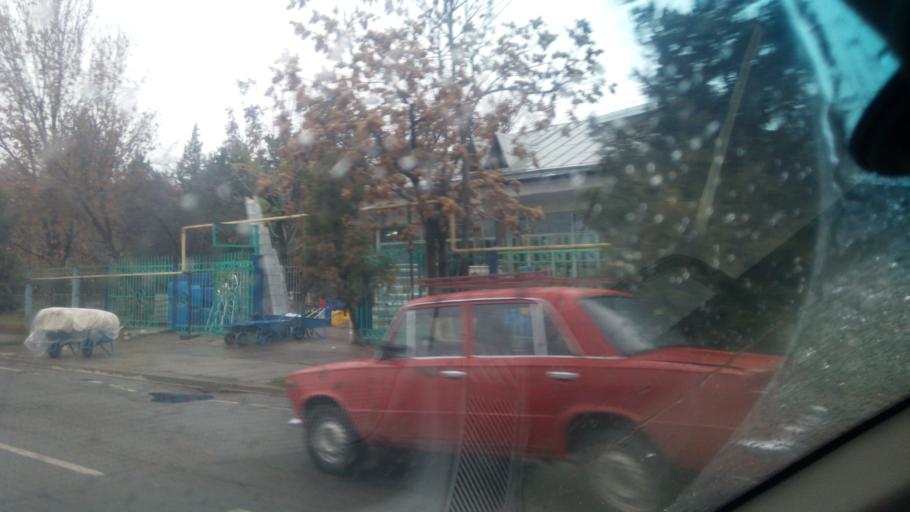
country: UZ
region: Toshkent Shahri
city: Bektemir
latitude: 41.2513
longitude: 69.3551
